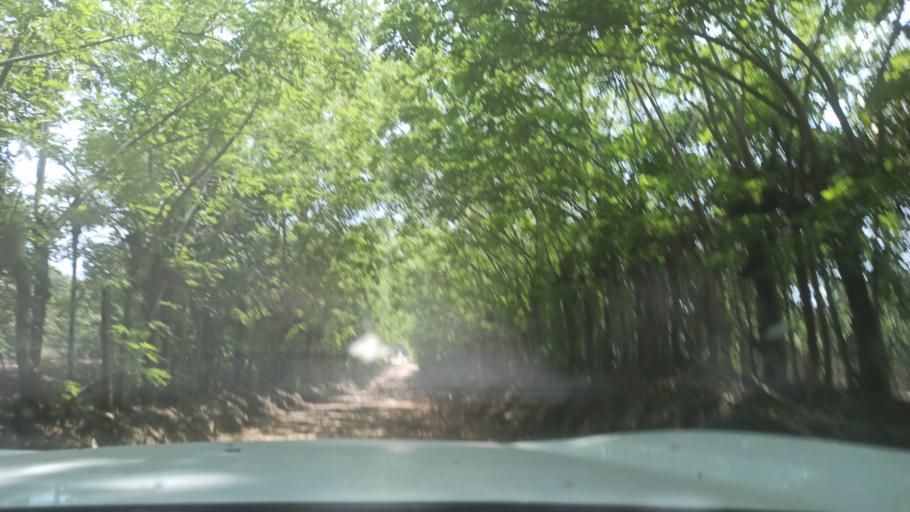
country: MX
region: Veracruz
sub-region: Atzalan
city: Colonias Pedernales
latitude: 20.0379
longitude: -97.0052
